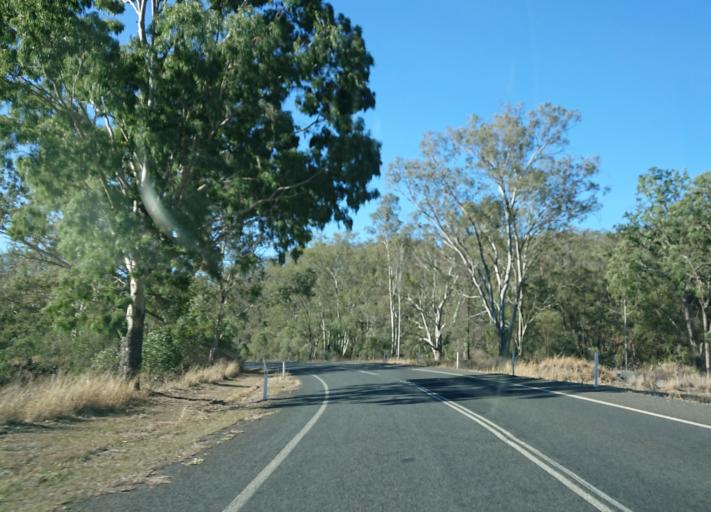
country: AU
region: Queensland
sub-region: Toowoomba
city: Rangeville
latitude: -27.7259
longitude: 152.1167
